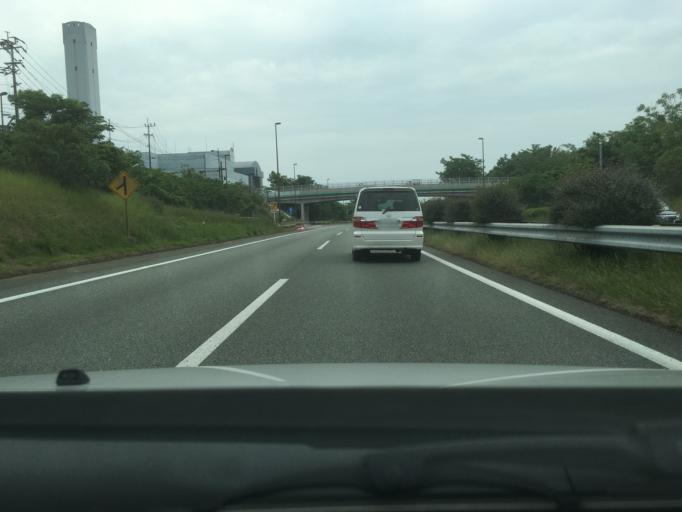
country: JP
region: Kumamoto
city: Ozu
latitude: 32.8089
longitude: 130.7938
